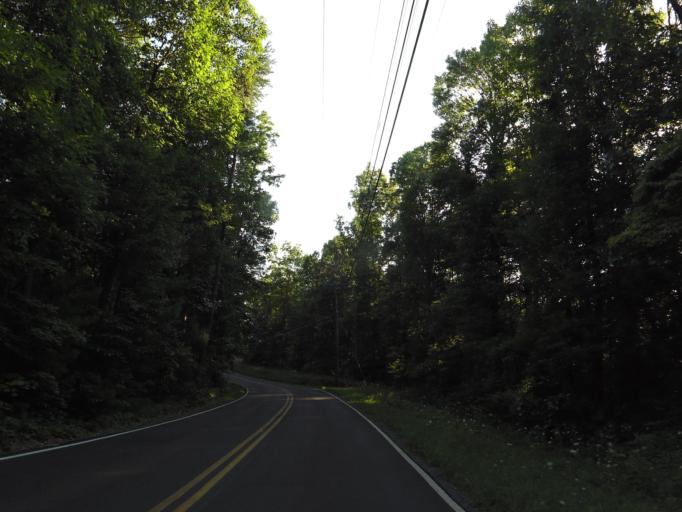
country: US
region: Tennessee
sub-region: Blount County
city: Maryville
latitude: 35.6401
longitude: -83.9219
